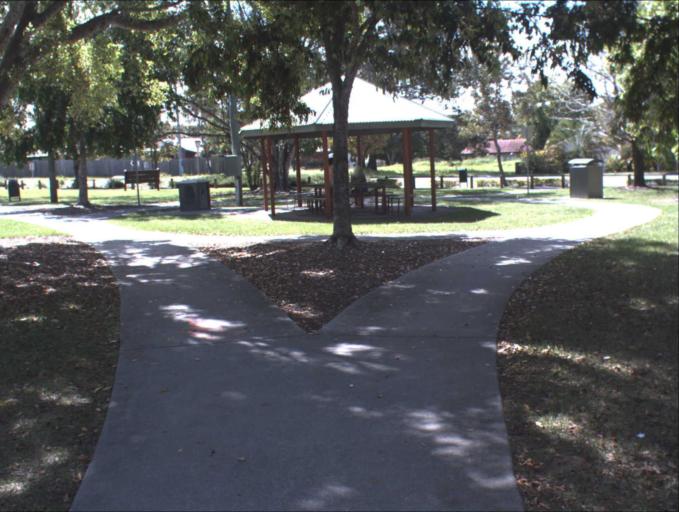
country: AU
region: Queensland
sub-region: Brisbane
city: Sunnybank Hills
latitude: -27.6643
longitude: 153.0250
